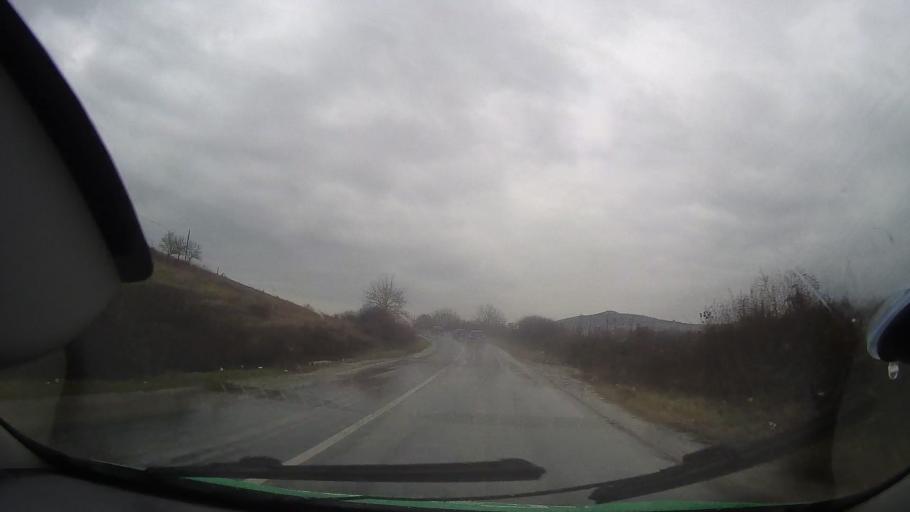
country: RO
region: Bihor
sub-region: Comuna Rabagani
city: Rabagani
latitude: 46.7550
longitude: 22.2062
